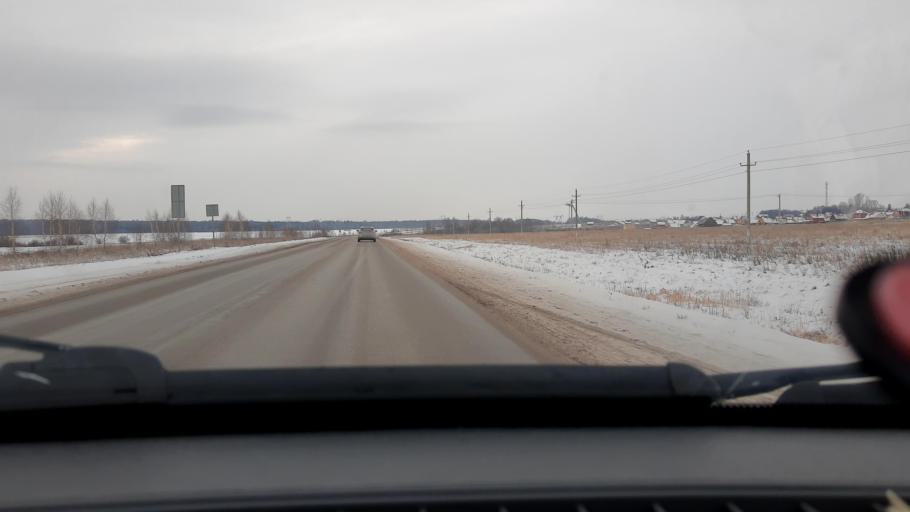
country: RU
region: Bashkortostan
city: Iglino
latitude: 54.7965
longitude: 56.4158
